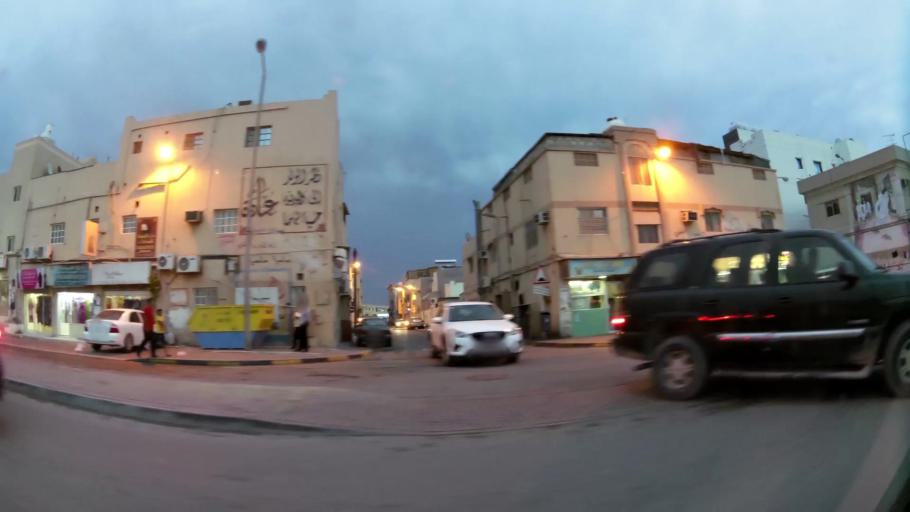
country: BH
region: Central Governorate
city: Madinat Hamad
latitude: 26.1454
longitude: 50.4962
